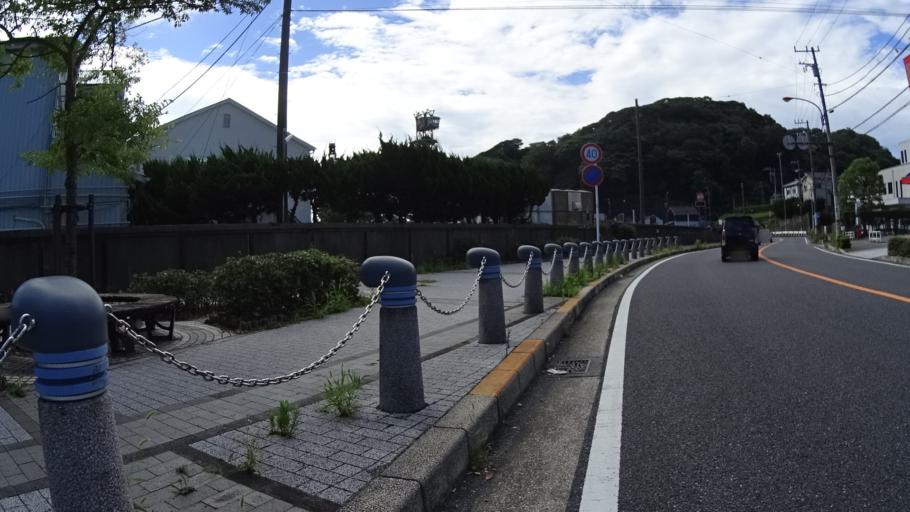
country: JP
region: Kanagawa
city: Yokosuka
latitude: 35.2459
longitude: 139.7155
